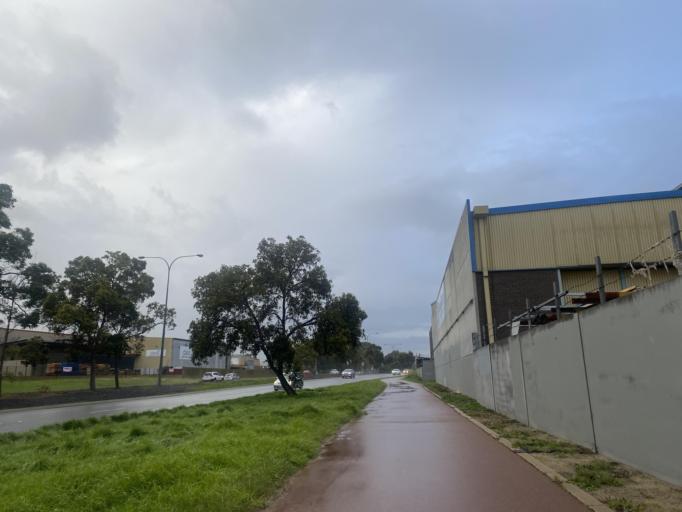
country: AU
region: Western Australia
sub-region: Canning
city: East Cannington
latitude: -32.0003
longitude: 115.9668
